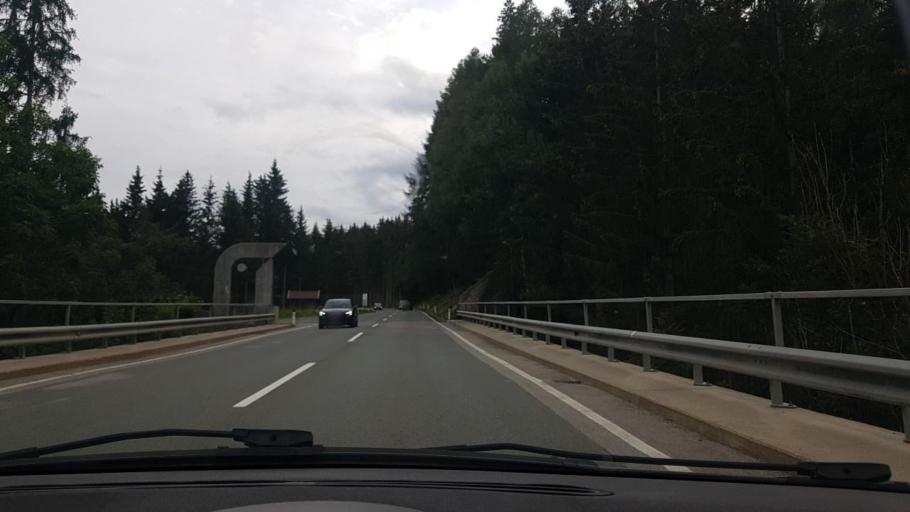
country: AT
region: Carinthia
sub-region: Politischer Bezirk Spittal an der Drau
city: Winklern
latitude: 46.8656
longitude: 12.8679
